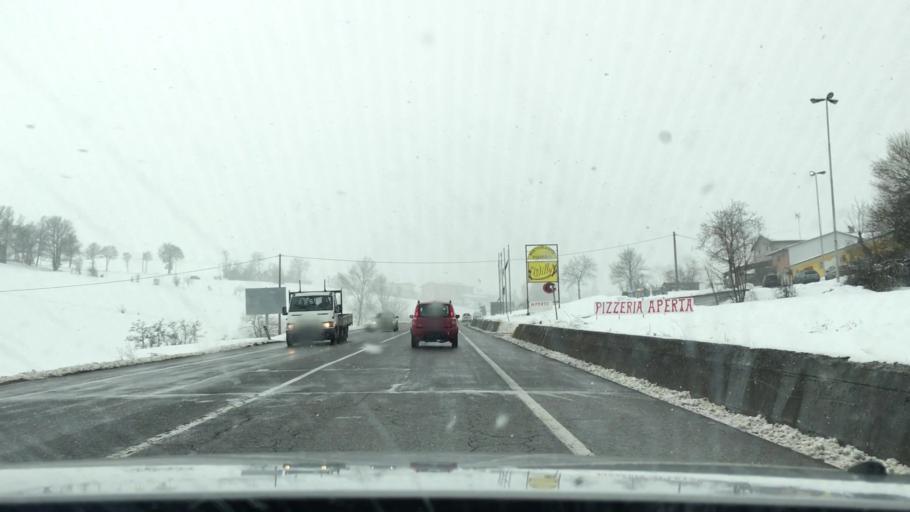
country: IT
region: Emilia-Romagna
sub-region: Provincia di Modena
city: Sant'Antonio
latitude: 44.4122
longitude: 10.8456
